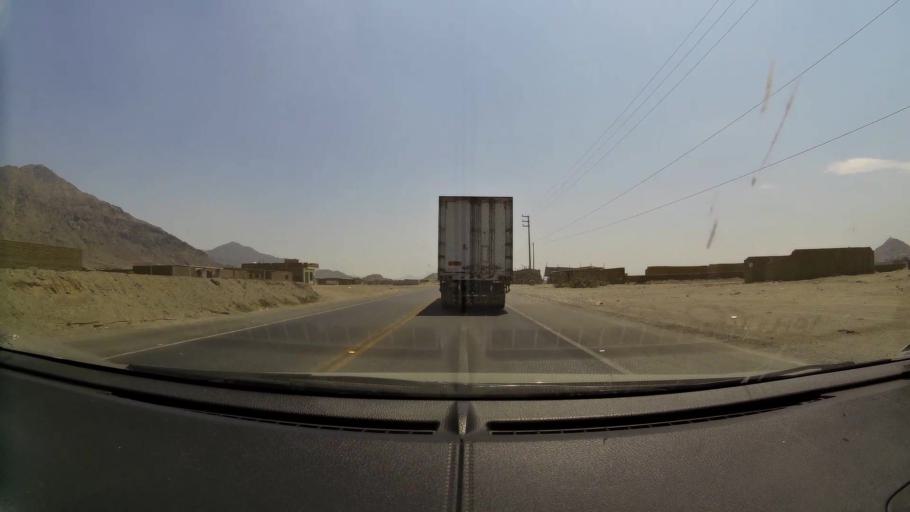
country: PE
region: La Libertad
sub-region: Provincia de Pacasmayo
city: Guadalupe
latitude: -7.2666
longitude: -79.4829
